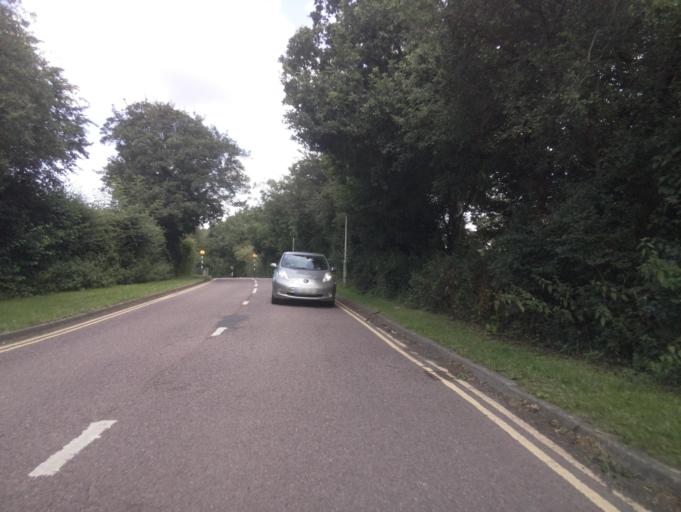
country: GB
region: England
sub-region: Wiltshire
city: Lydiard Tregoze
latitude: 51.5593
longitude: -1.8426
